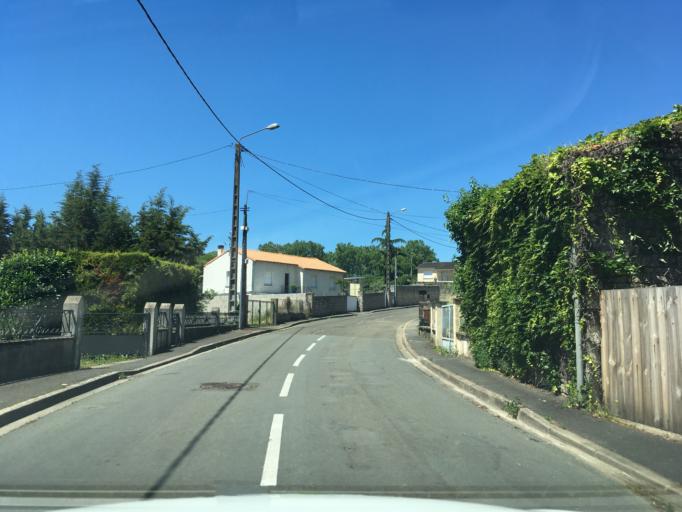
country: FR
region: Poitou-Charentes
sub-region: Departement des Deux-Sevres
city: Niort
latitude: 46.3322
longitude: -0.4288
